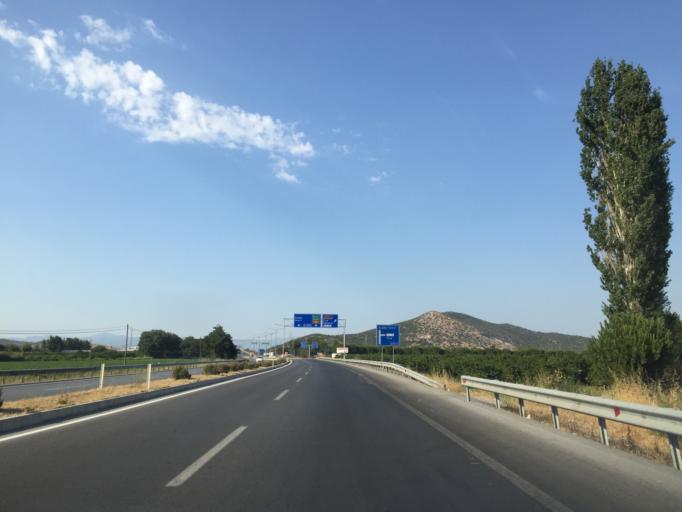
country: TR
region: Izmir
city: Belevi
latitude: 38.0180
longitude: 27.4393
